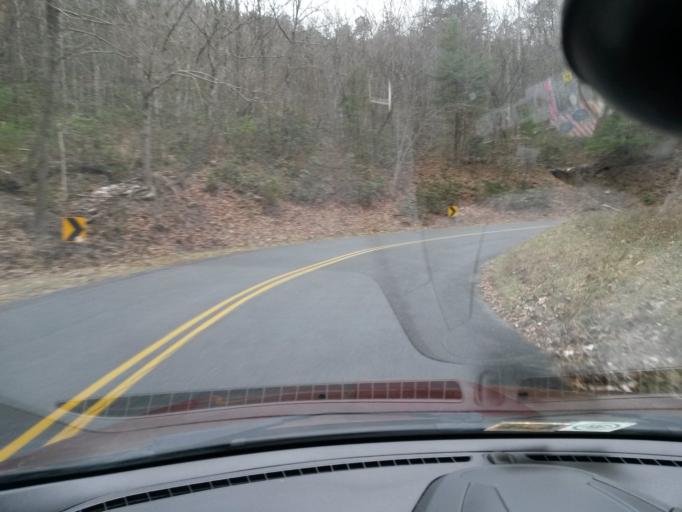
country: US
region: Virginia
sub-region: City of Lexington
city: Lexington
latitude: 37.8924
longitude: -79.5811
